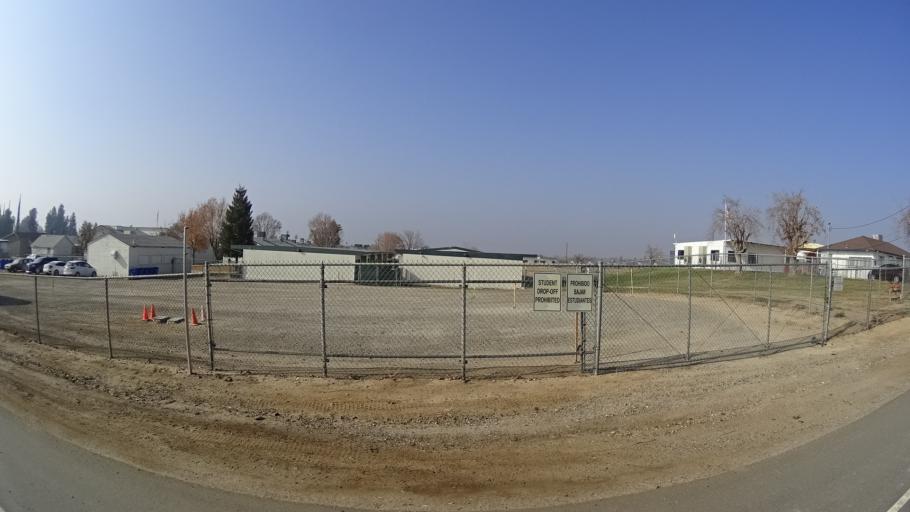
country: US
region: California
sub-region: Kern County
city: Lamont
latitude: 35.3666
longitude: -118.8964
